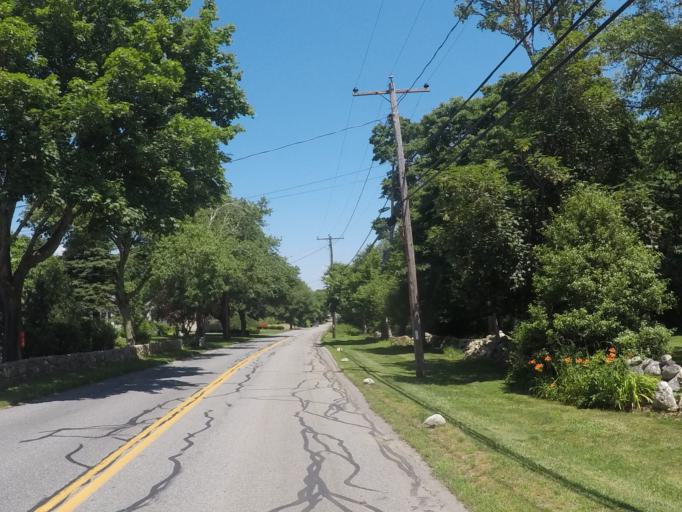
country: US
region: Massachusetts
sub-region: Bristol County
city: Bliss Corner
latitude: 41.5493
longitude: -70.9555
